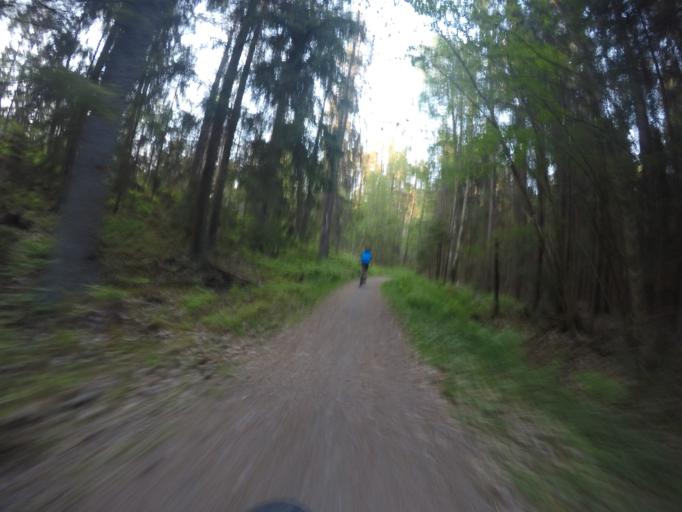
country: SE
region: Soedermanland
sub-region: Eskilstuna Kommun
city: Skogstorp
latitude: 59.3351
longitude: 16.4932
